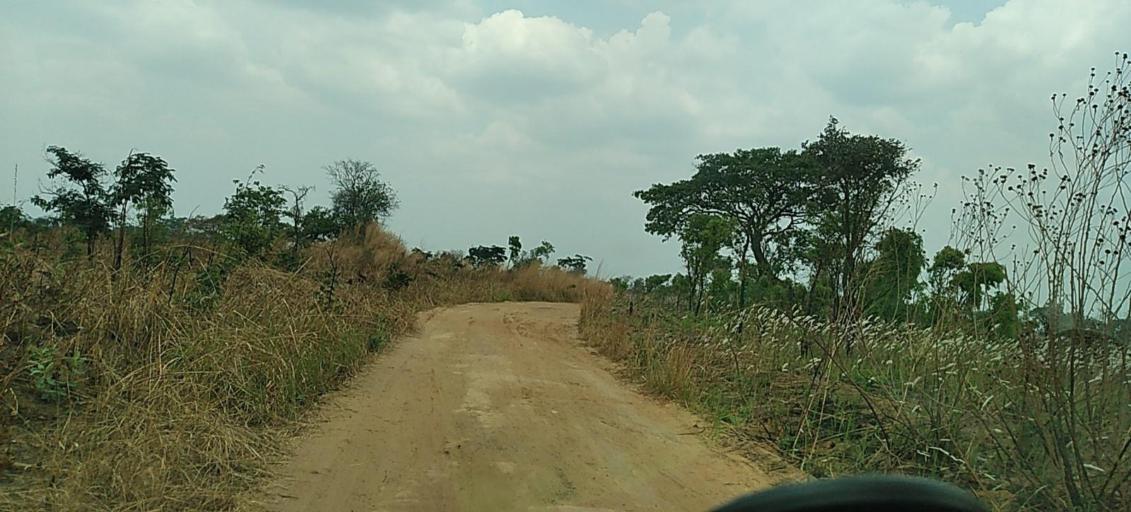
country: ZM
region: North-Western
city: Kansanshi
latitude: -12.0830
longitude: 26.3661
